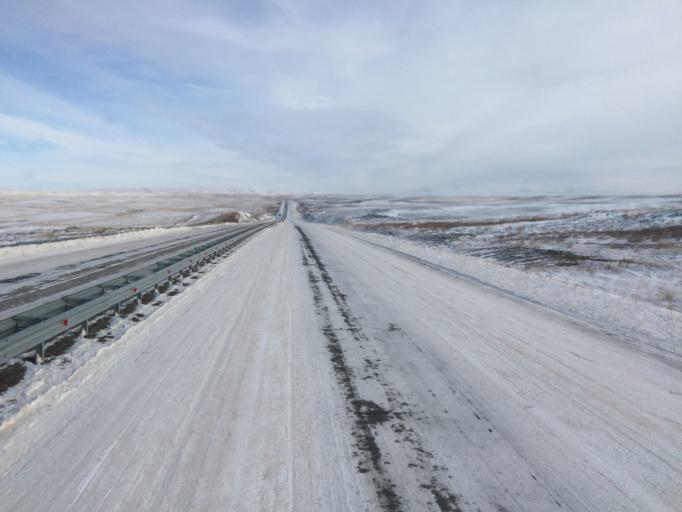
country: KZ
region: Zhambyl
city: Georgiyevka
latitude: 43.3629
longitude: 74.6865
